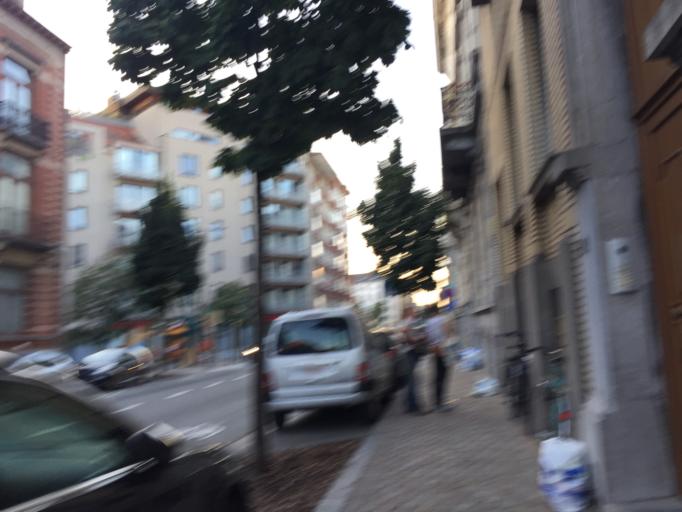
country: BE
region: Brussels Capital
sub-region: Bruxelles-Capitale
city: Brussels
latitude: 50.8321
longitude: 4.3762
